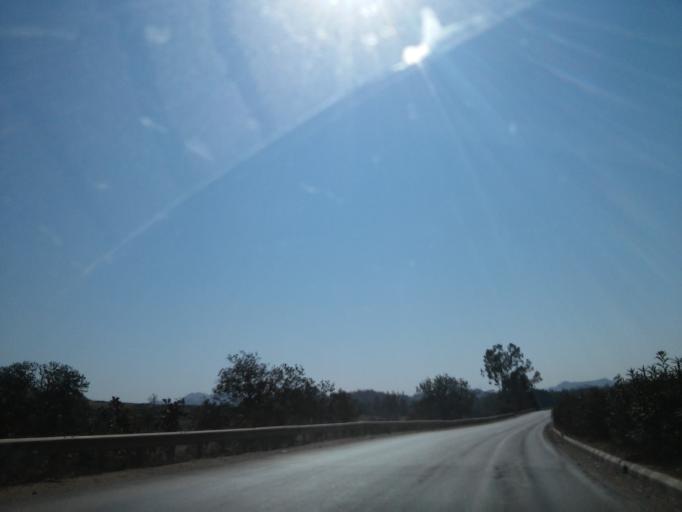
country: IN
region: Rajasthan
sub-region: Dungarpur
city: Dungarpur
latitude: 24.1186
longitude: 73.6966
